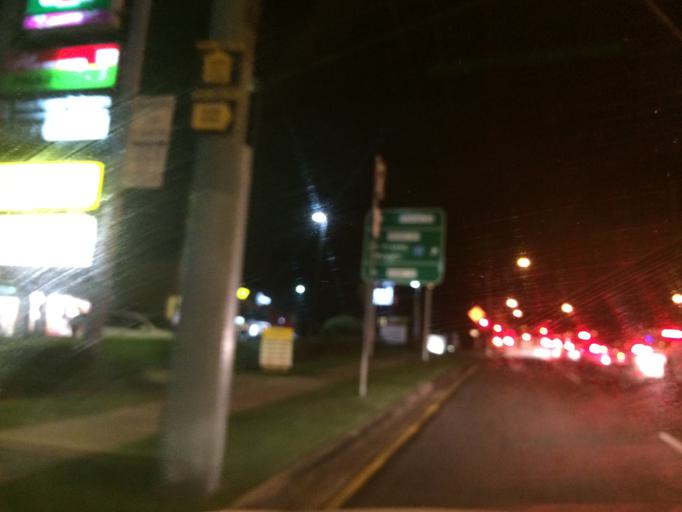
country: AU
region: Queensland
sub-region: Brisbane
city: Kenmore Hills
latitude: -27.5095
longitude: 152.9382
